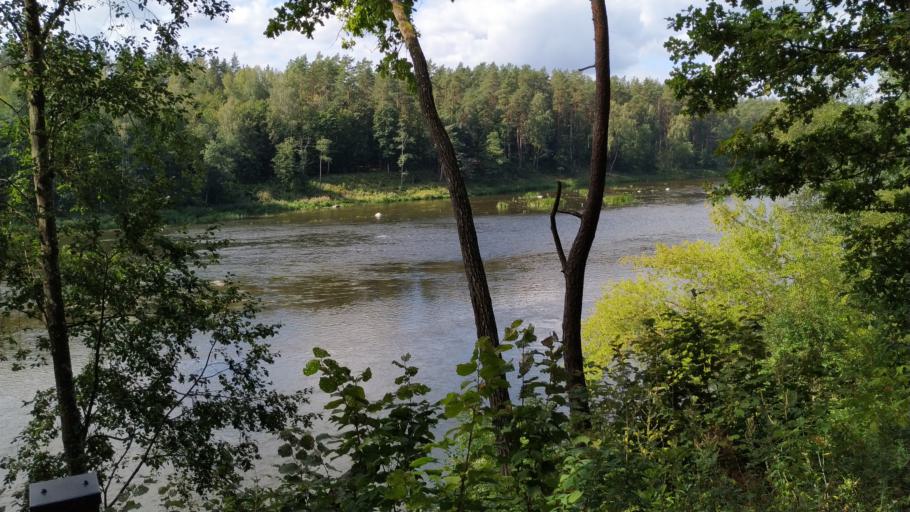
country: LT
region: Vilnius County
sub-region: Vilniaus Rajonas
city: Vievis
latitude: 54.8090
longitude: 24.9656
